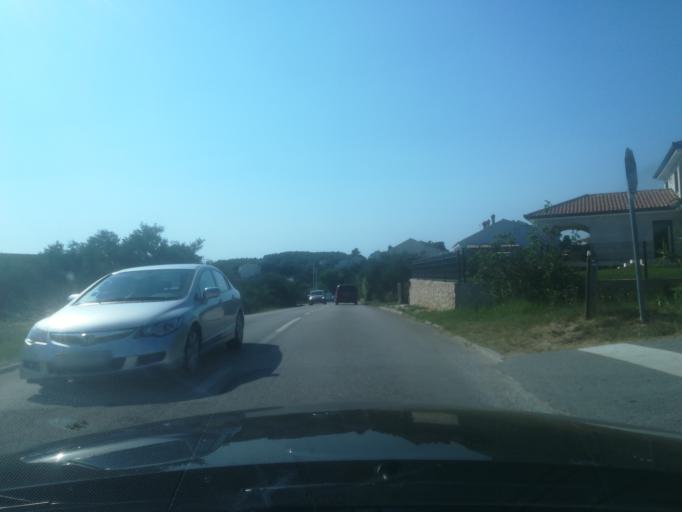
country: HR
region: Primorsko-Goranska
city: Banjol
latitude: 44.7517
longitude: 14.7830
